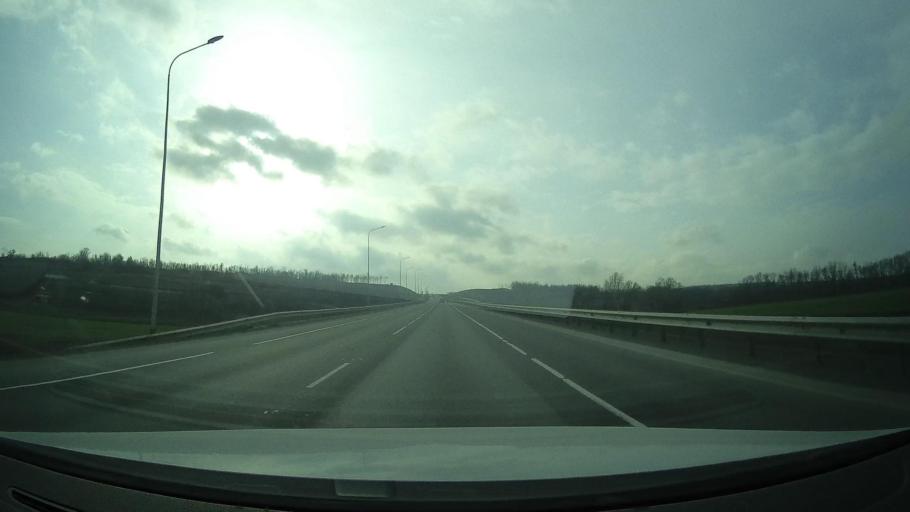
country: RU
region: Rostov
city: Grushevskaya
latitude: 47.4376
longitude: 39.8718
